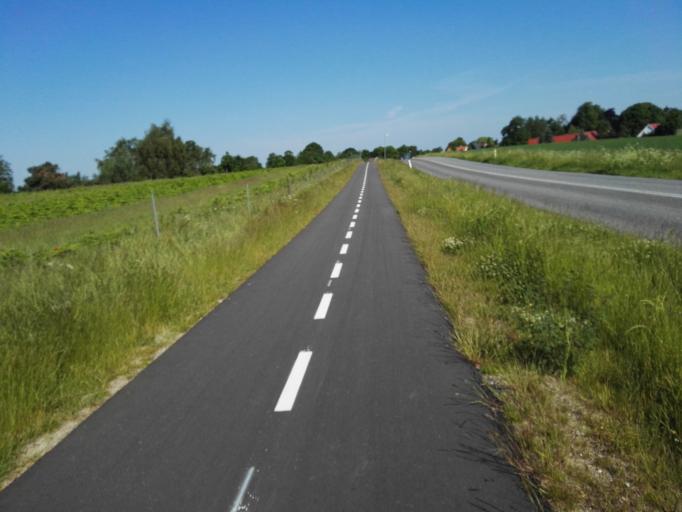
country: DK
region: Zealand
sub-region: Lejre Kommune
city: Ejby
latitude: 55.7151
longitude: 11.8921
